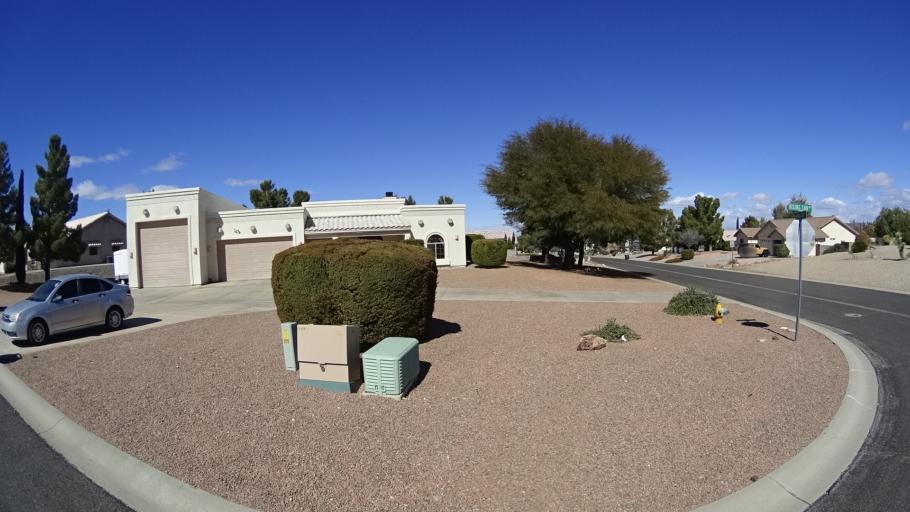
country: US
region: Arizona
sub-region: Mohave County
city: Kingman
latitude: 35.1977
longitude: -113.9621
